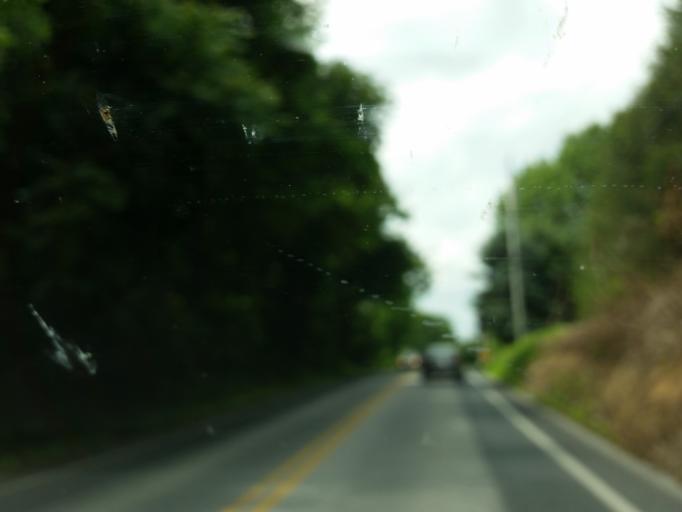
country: US
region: Delaware
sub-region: New Castle County
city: Newark
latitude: 39.7292
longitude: -75.7914
